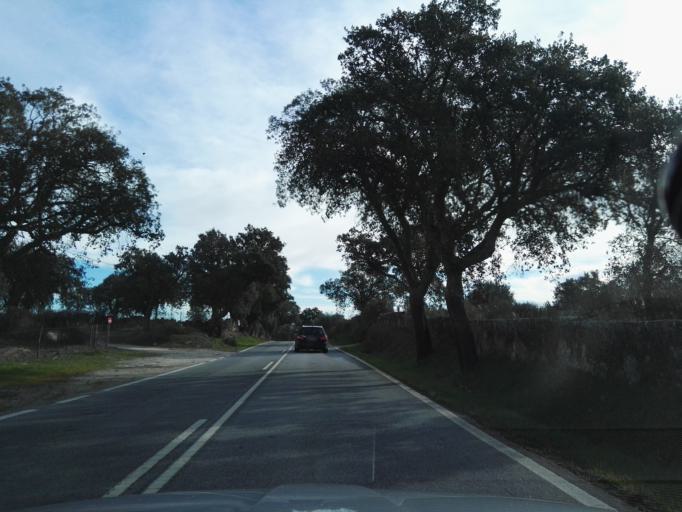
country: PT
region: Portalegre
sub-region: Nisa
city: Nisa
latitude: 39.5000
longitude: -7.6786
